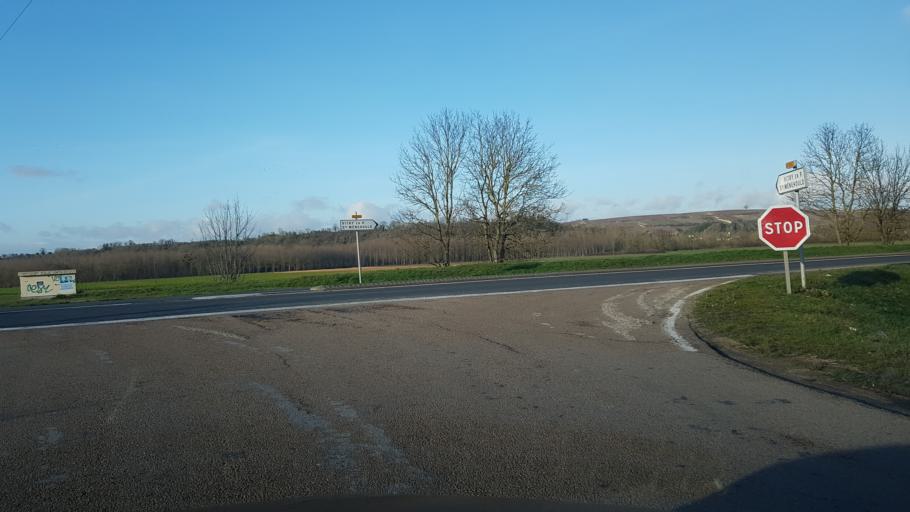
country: FR
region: Champagne-Ardenne
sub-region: Departement de la Marne
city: Vitry-le-Francois
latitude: 48.7365
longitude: 4.6130
